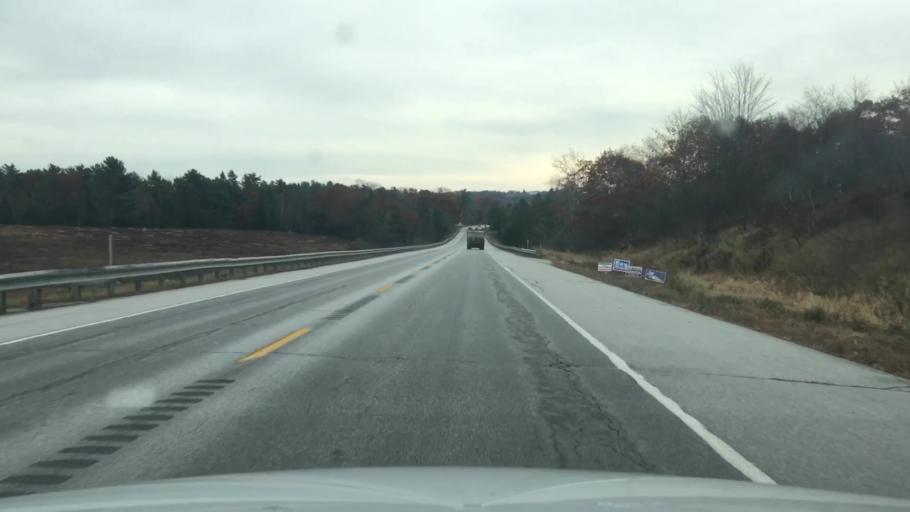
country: US
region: Maine
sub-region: Hancock County
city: Orland
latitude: 44.5699
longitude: -68.7245
